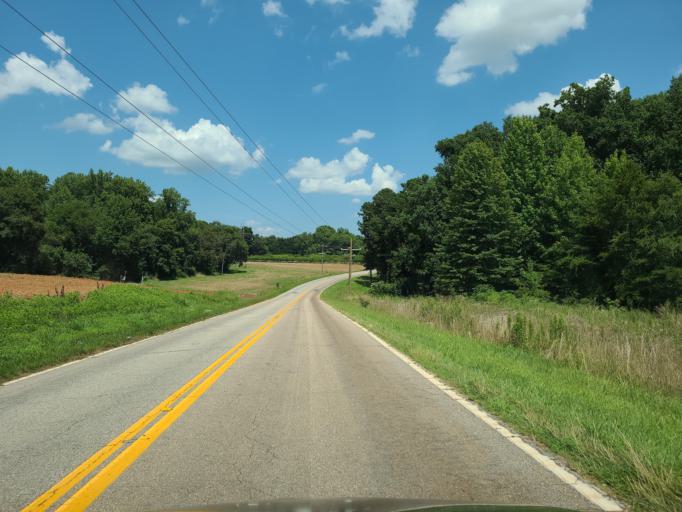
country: US
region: South Carolina
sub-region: Spartanburg County
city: Inman Mills
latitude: 35.0366
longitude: -82.1348
